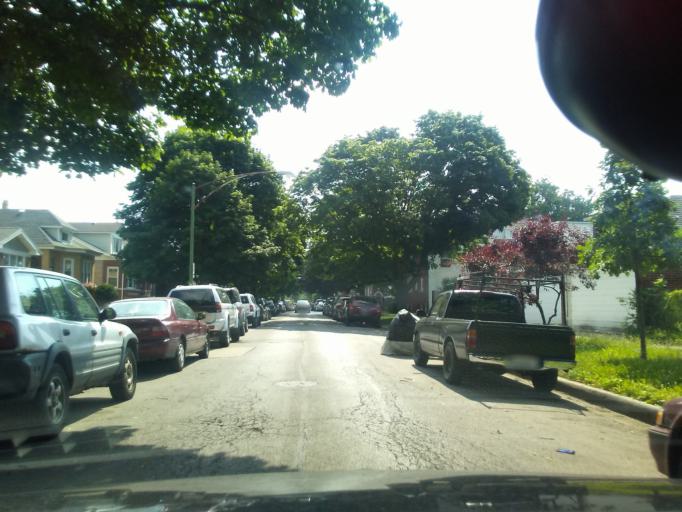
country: US
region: Illinois
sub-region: Cook County
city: Oak Park
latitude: 41.9223
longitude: -87.7557
